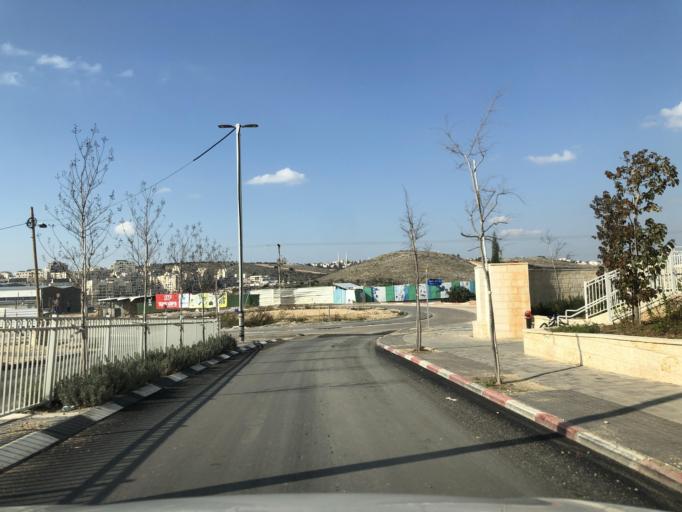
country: IL
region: Jerusalem
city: Modiin Ilit
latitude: 31.9346
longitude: 35.0523
